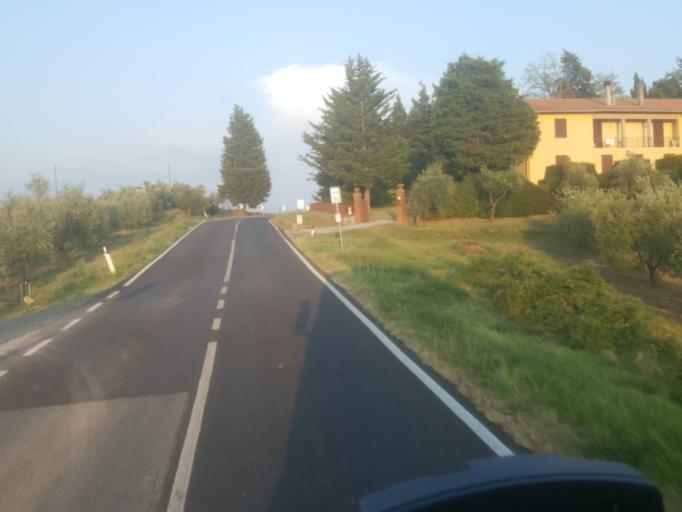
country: IT
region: Tuscany
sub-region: Province of Florence
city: Gambassi Terme
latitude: 43.5451
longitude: 10.9721
